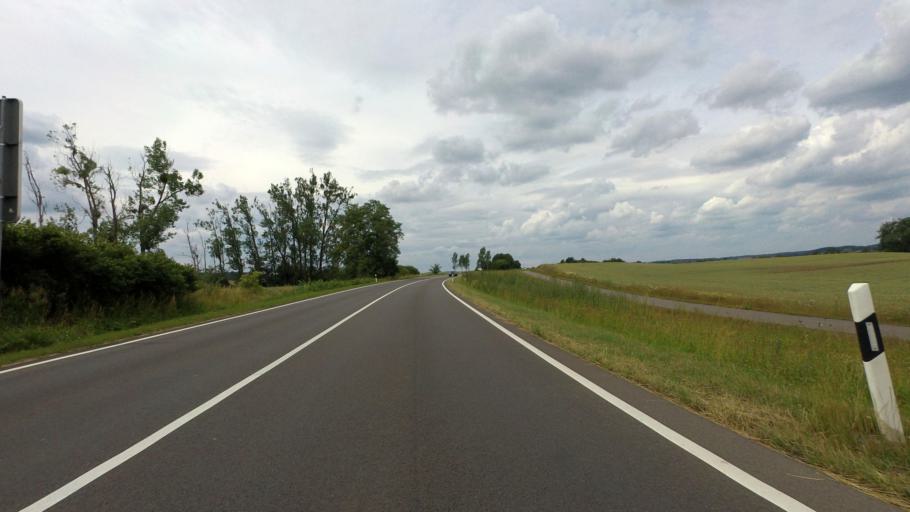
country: DE
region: Brandenburg
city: Chorin
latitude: 52.9582
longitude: 13.9223
